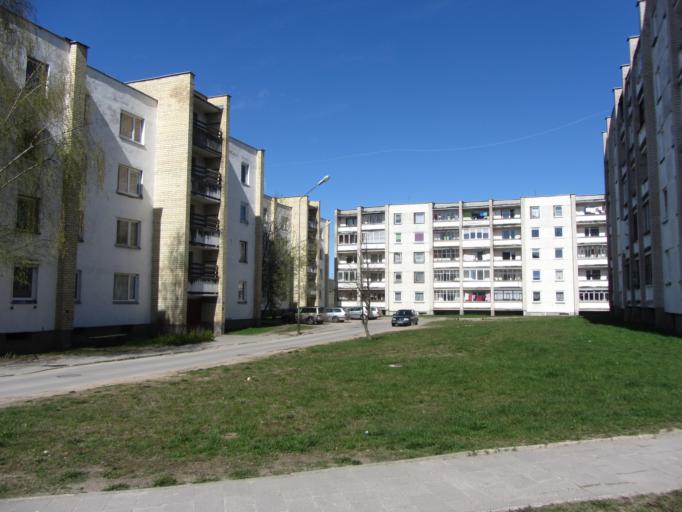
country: LT
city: Zarasai
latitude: 55.7385
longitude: 26.2642
